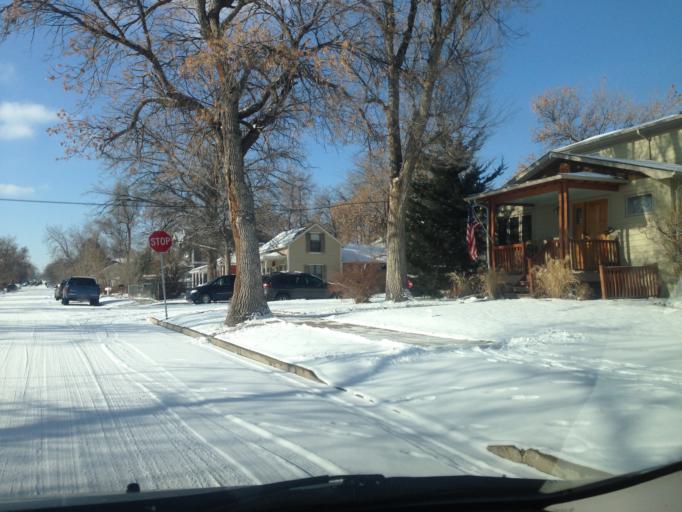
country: US
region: Colorado
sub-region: Boulder County
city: Lafayette
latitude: 39.9963
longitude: -105.0864
